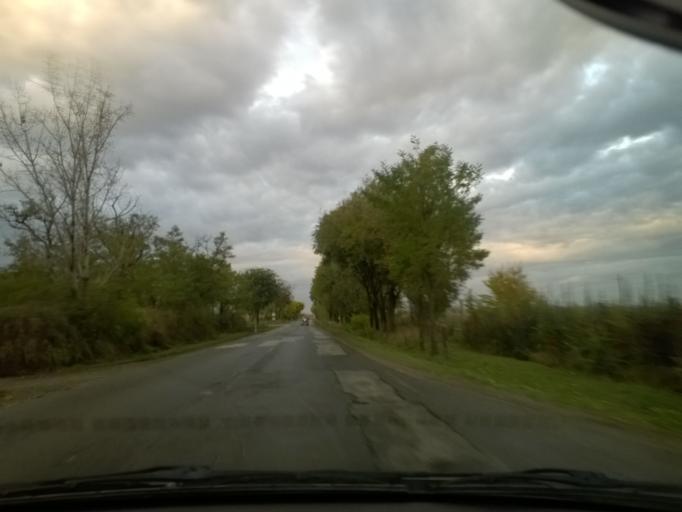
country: HU
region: Bacs-Kiskun
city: Solt
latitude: 46.8211
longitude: 19.0070
